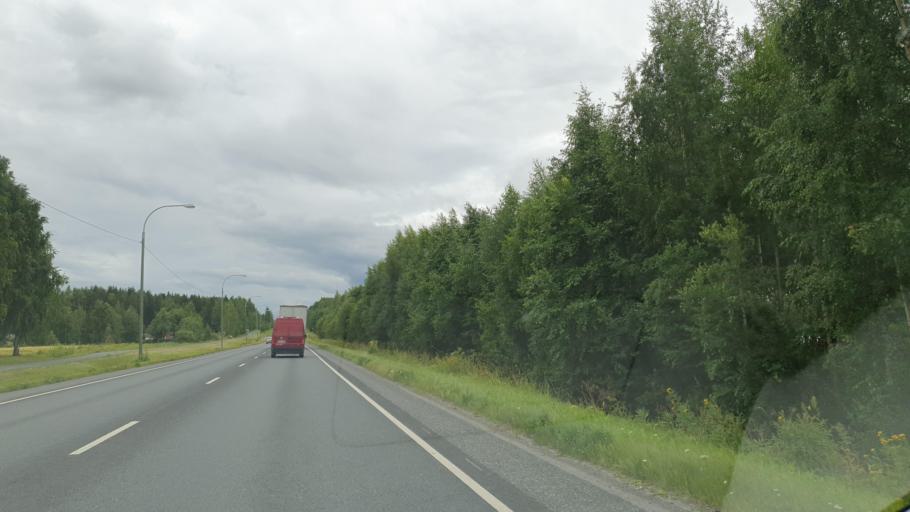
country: FI
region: Northern Savo
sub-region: Ylae-Savo
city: Lapinlahti
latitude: 63.4525
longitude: 27.3181
